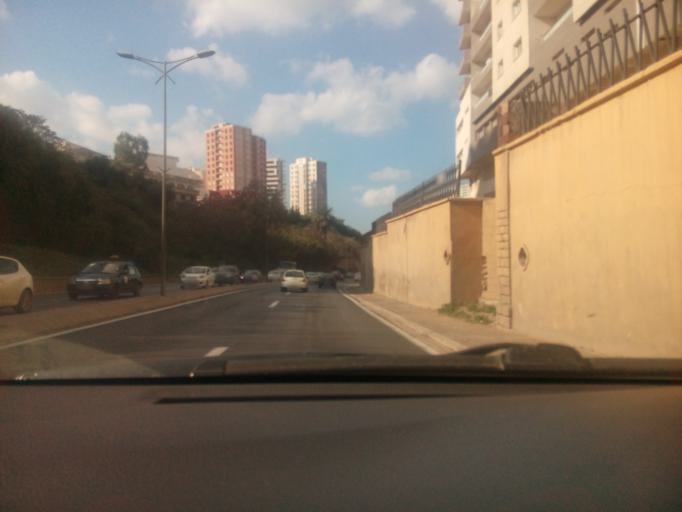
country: DZ
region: Oran
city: Oran
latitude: 35.7043
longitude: -0.6205
